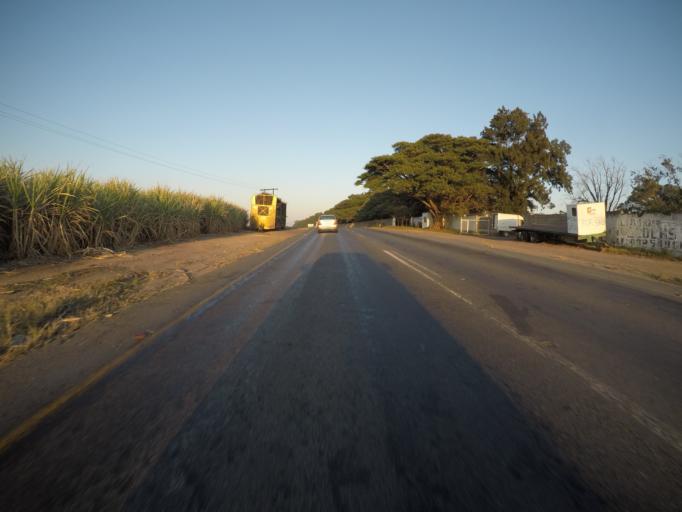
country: ZA
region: KwaZulu-Natal
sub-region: uThungulu District Municipality
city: eSikhawini
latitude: -28.8226
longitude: 31.8783
